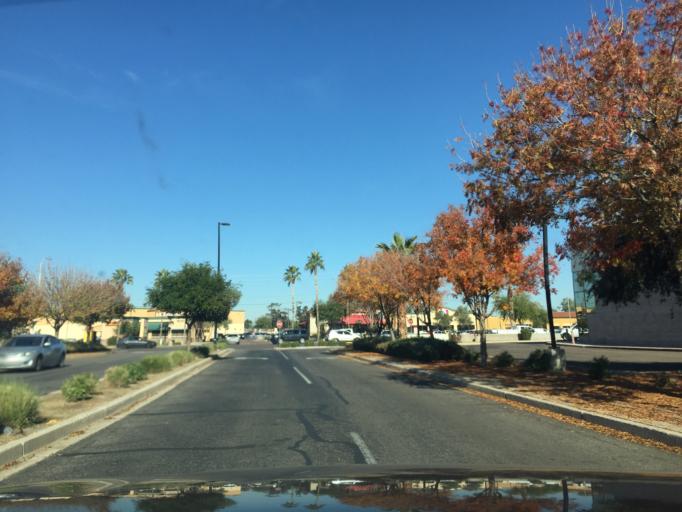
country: US
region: Arizona
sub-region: Maricopa County
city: Tolleson
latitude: 33.4794
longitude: -112.2227
